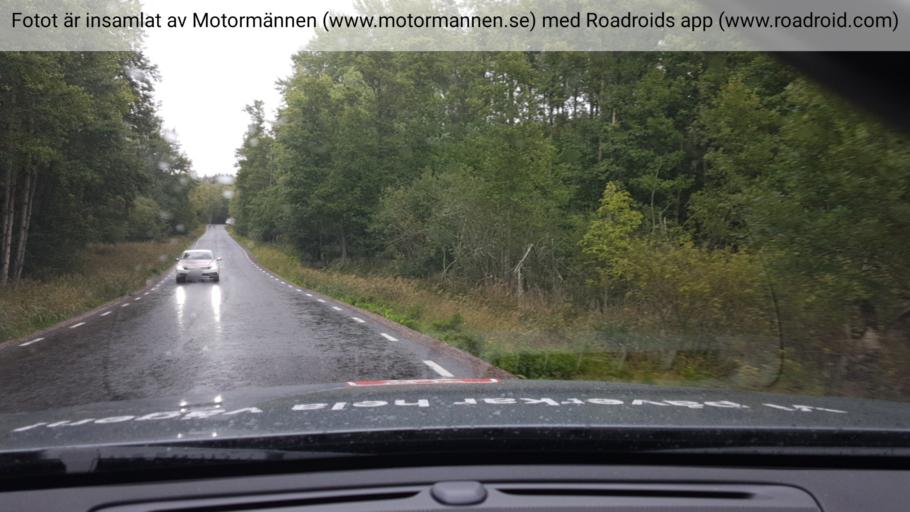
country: SE
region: Stockholm
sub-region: Nynashamns Kommun
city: Osmo
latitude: 59.0387
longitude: 17.9202
